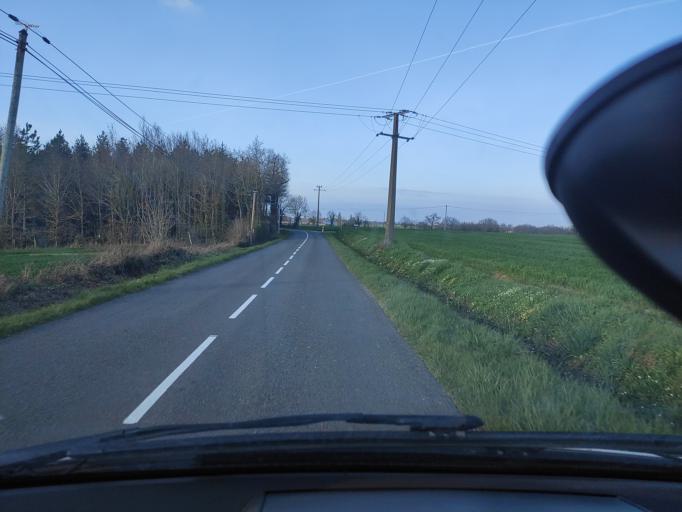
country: FR
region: Pays de la Loire
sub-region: Departement de la Vendee
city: La Chaize-le-Vicomte
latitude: 46.6401
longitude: -1.2997
